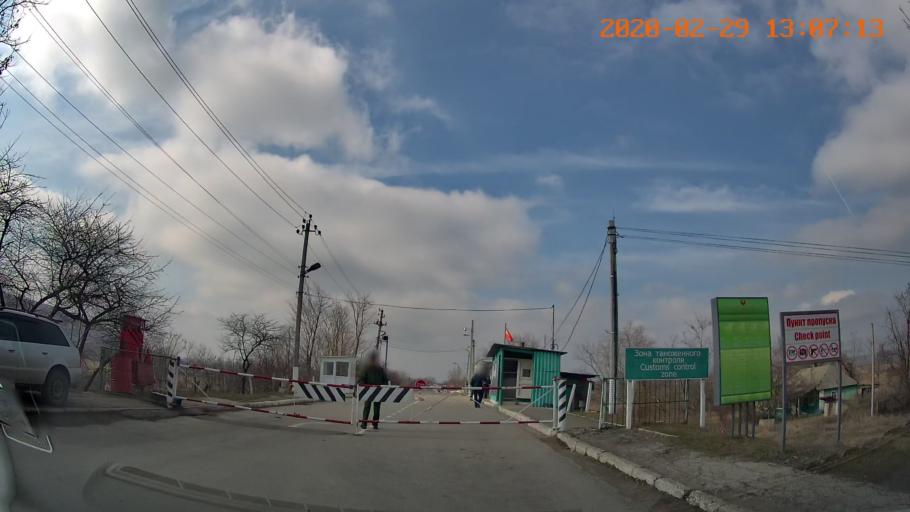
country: MD
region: Telenesti
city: Camenca
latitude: 48.0108
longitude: 28.7052
